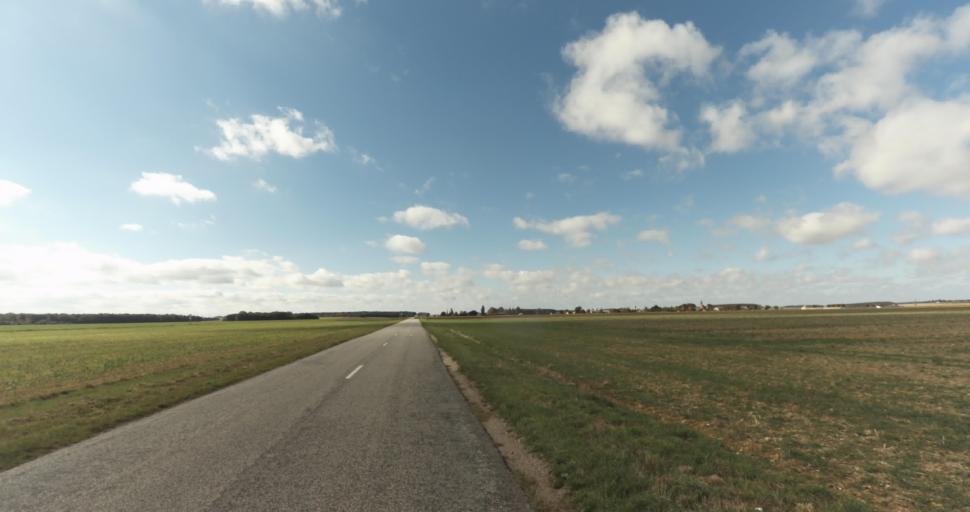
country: FR
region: Centre
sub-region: Departement d'Eure-et-Loir
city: Garnay
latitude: 48.7048
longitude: 1.2986
